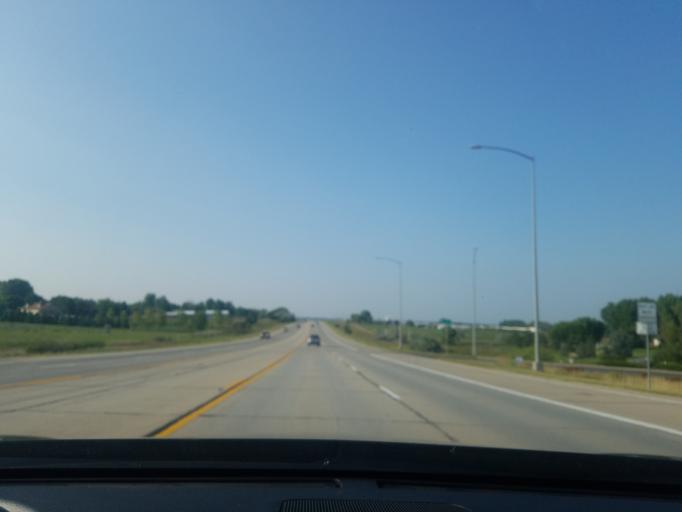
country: US
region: Colorado
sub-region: Larimer County
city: Campion
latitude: 40.3581
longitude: -105.0737
